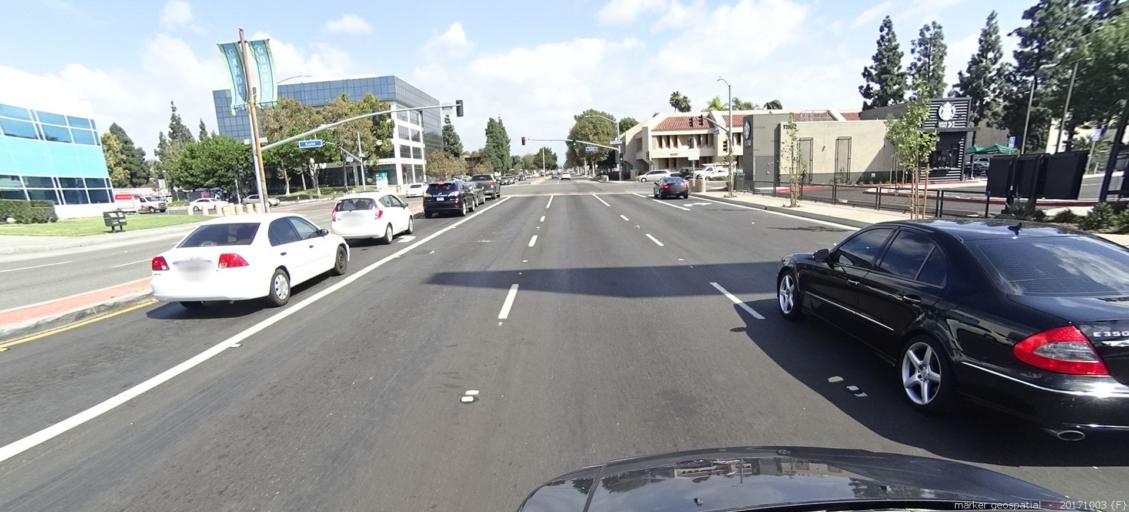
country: US
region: California
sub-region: Orange County
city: Garden Grove
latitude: 33.7741
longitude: -117.9387
